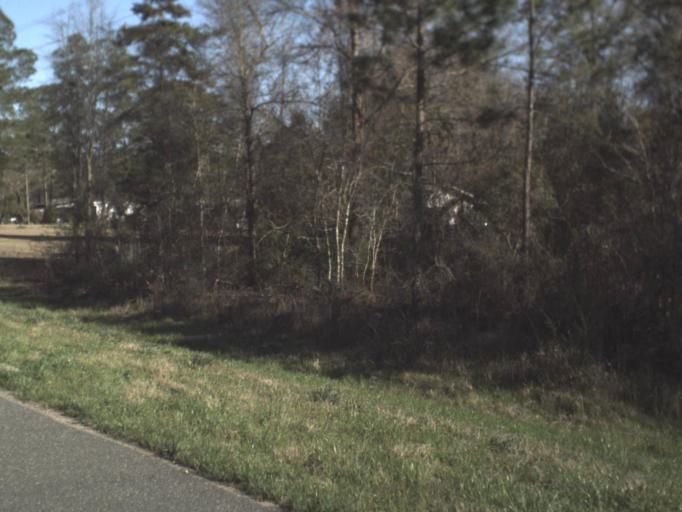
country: US
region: Florida
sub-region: Washington County
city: Chipley
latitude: 30.7874
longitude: -85.4362
